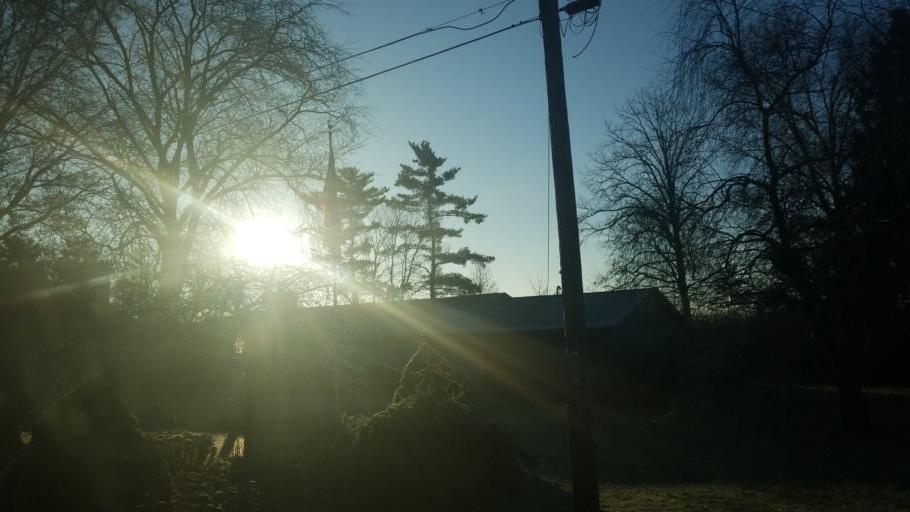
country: US
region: Ohio
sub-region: Marion County
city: Marion
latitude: 40.5717
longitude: -83.1116
